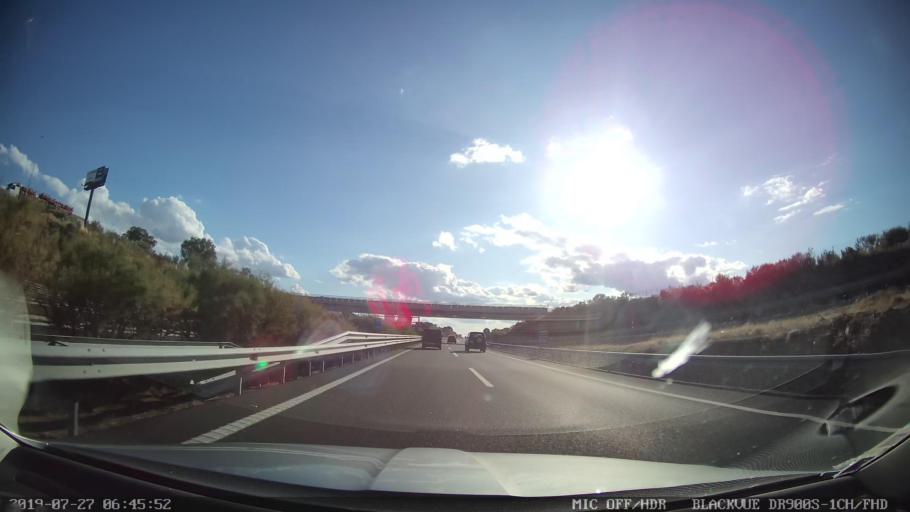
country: ES
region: Extremadura
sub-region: Provincia de Caceres
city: Navalmoral de la Mata
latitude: 39.8743
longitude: -5.5507
